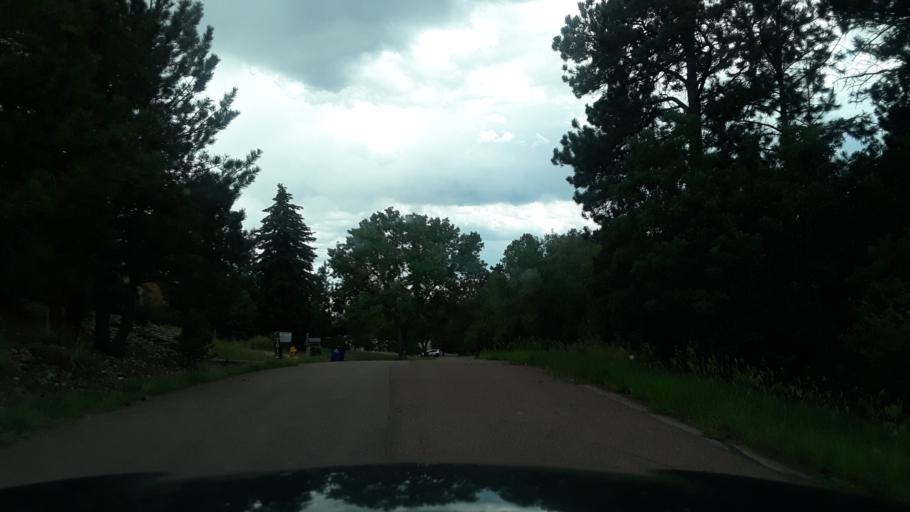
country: US
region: Colorado
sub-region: El Paso County
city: Air Force Academy
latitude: 38.9456
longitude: -104.8225
